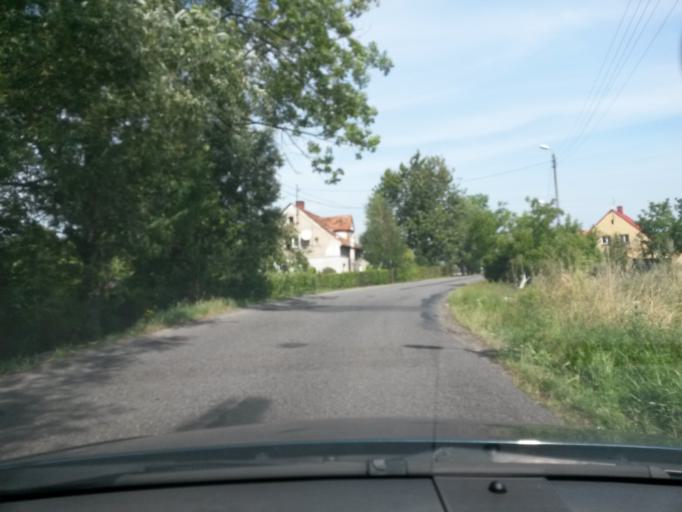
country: PL
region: Lower Silesian Voivodeship
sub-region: Powiat legnicki
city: Prochowice
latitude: 51.2462
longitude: 16.3628
